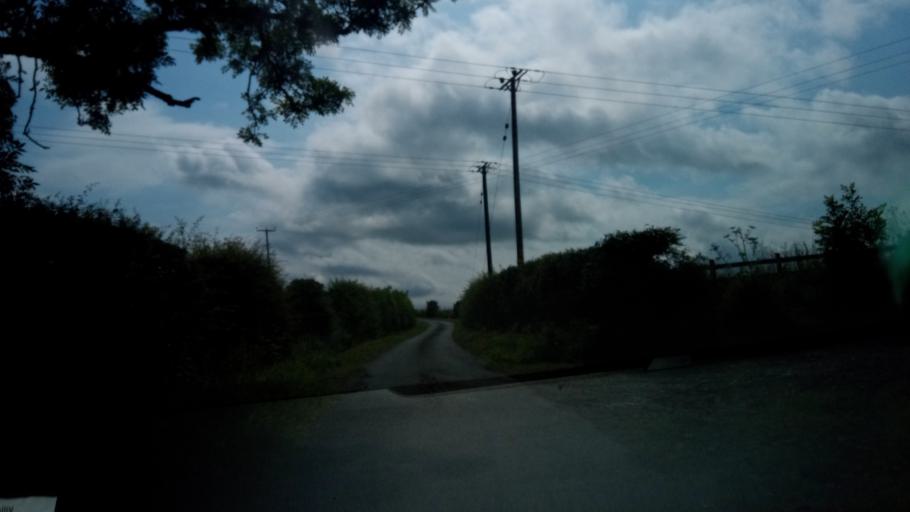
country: GB
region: Scotland
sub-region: The Scottish Borders
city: Jedburgh
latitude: 55.4629
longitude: -2.6394
